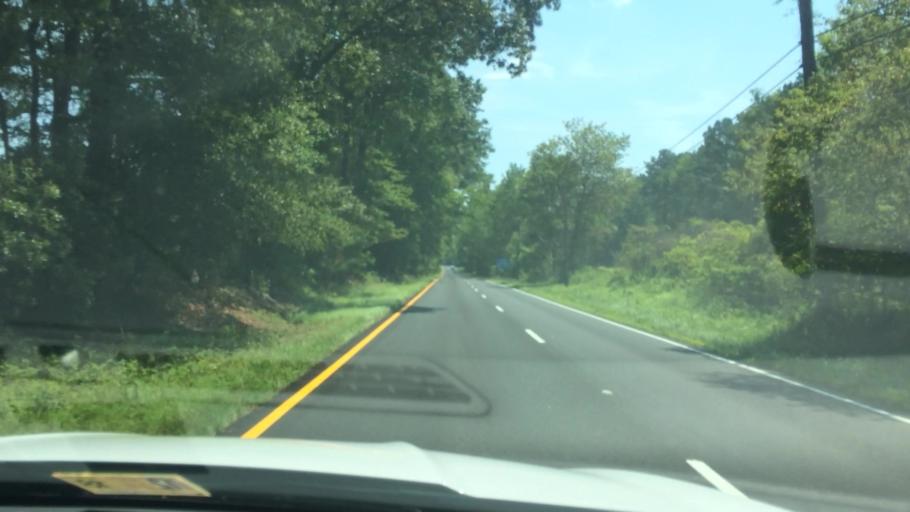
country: US
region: Virginia
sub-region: Charles City County
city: Charles City
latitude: 37.4449
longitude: -77.0565
